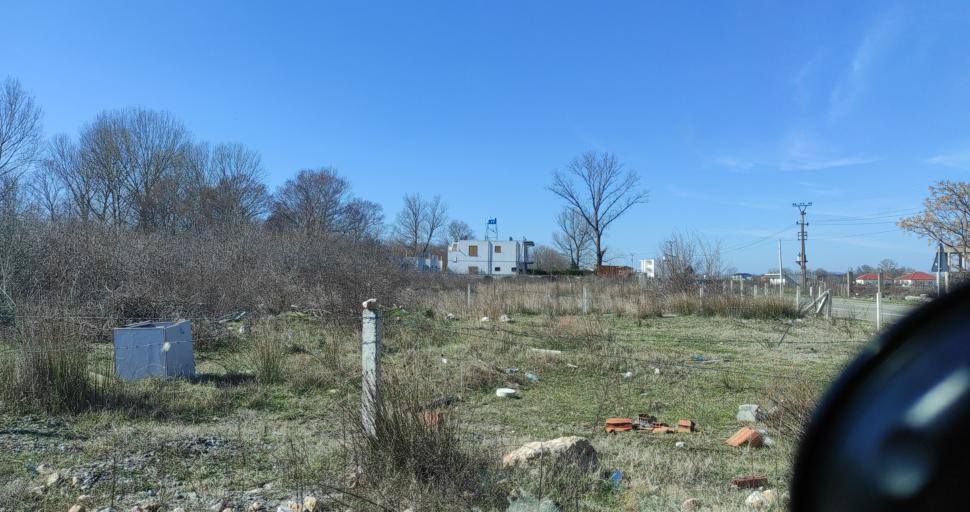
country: AL
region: Shkoder
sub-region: Rrethi i Shkodres
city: Velipoje
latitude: 41.8671
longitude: 19.4108
